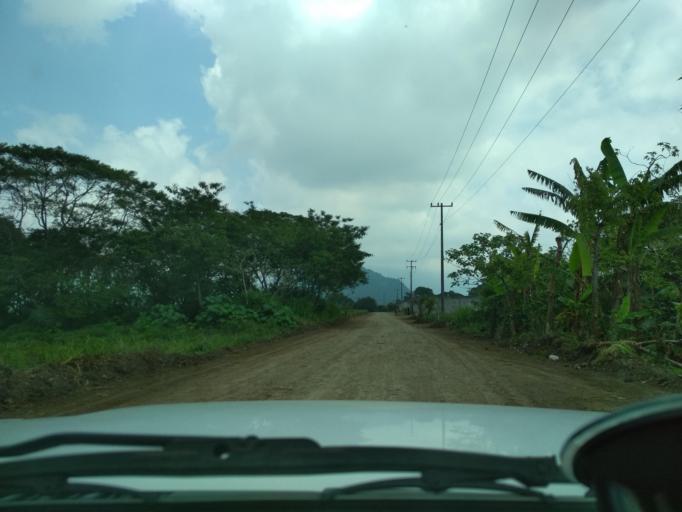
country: MX
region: Veracruz
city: Atzacan
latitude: 18.8794
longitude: -97.0786
